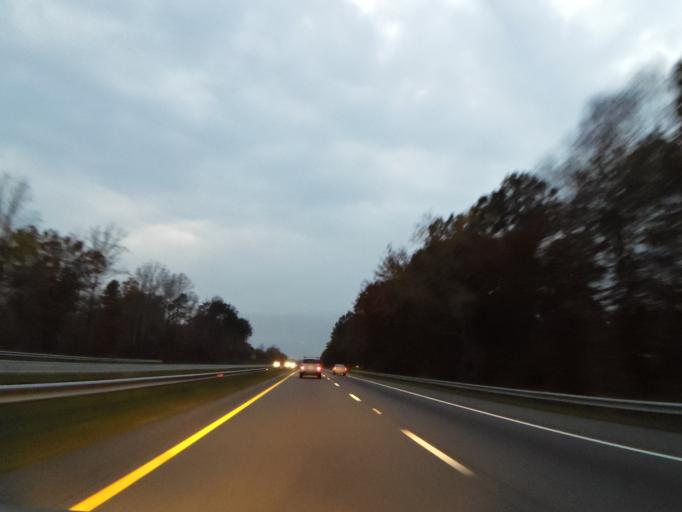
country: US
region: North Carolina
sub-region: McDowell County
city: West Marion
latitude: 35.6355
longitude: -82.0710
